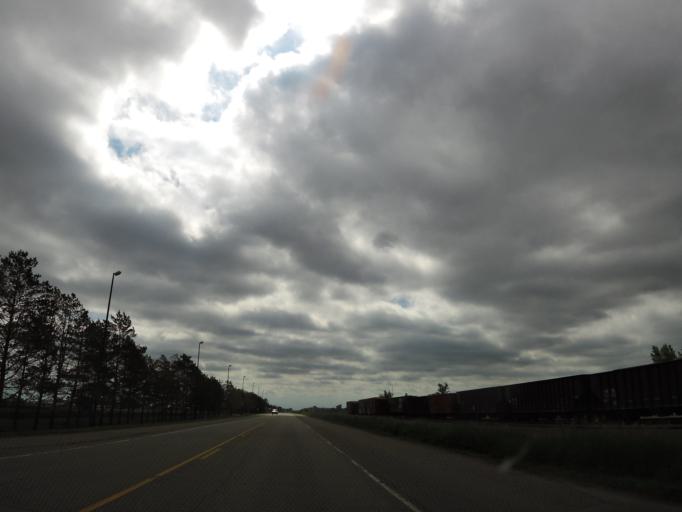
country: US
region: Minnesota
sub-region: Polk County
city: East Grand Forks
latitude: 47.9232
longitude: -97.0043
